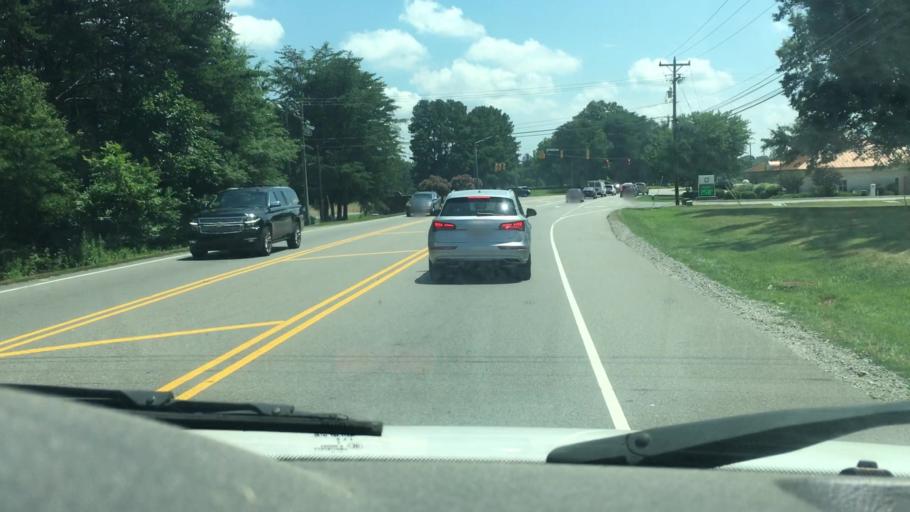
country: US
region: North Carolina
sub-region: Iredell County
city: Mooresville
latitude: 35.5805
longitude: -80.8400
